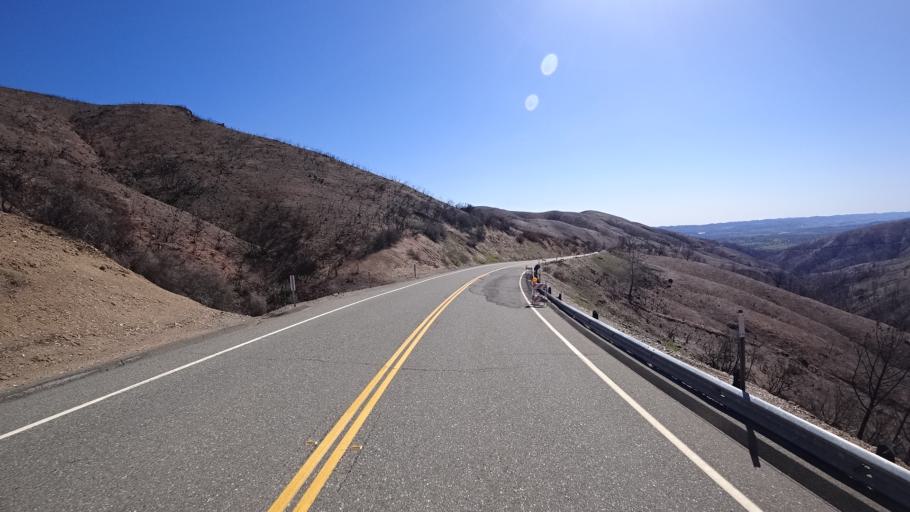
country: US
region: California
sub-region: Tehama County
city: Rancho Tehama Reserve
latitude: 39.6596
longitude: -122.6283
